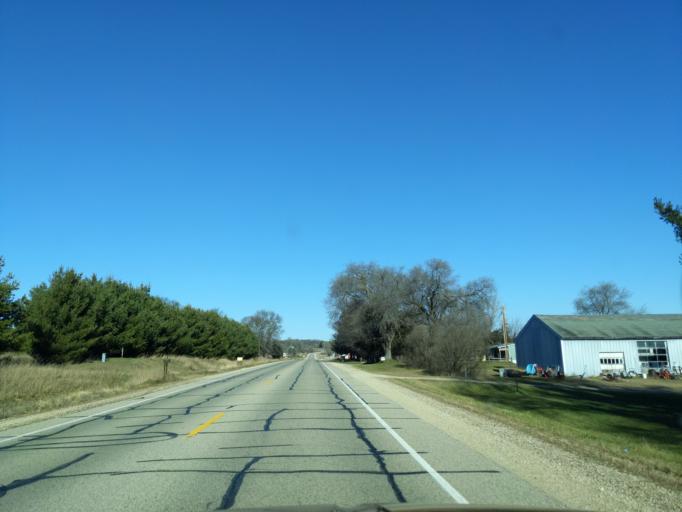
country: US
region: Wisconsin
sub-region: Waushara County
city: Wautoma
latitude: 44.0957
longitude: -89.2912
